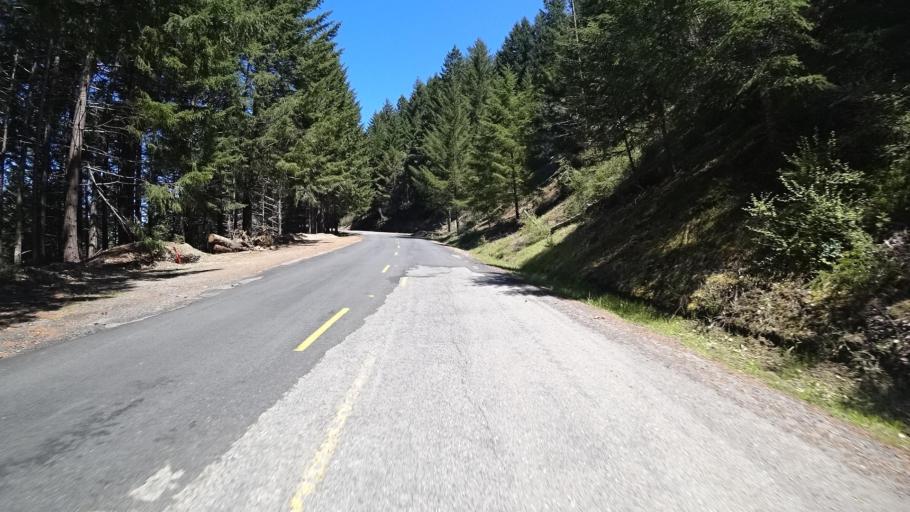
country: US
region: California
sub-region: Humboldt County
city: Rio Dell
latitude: 40.3017
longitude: -124.0584
